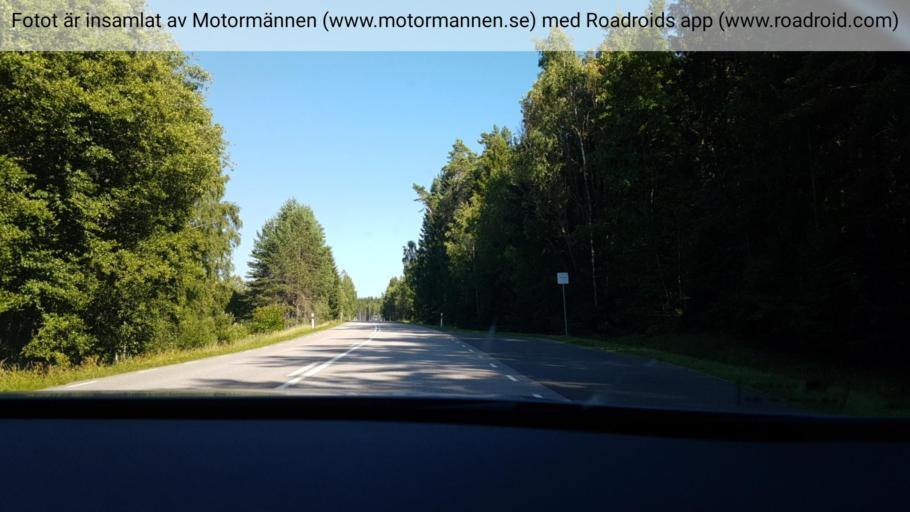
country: SE
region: Vaestra Goetaland
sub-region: Skara Kommun
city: Skara
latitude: 58.3127
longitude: 13.4488
